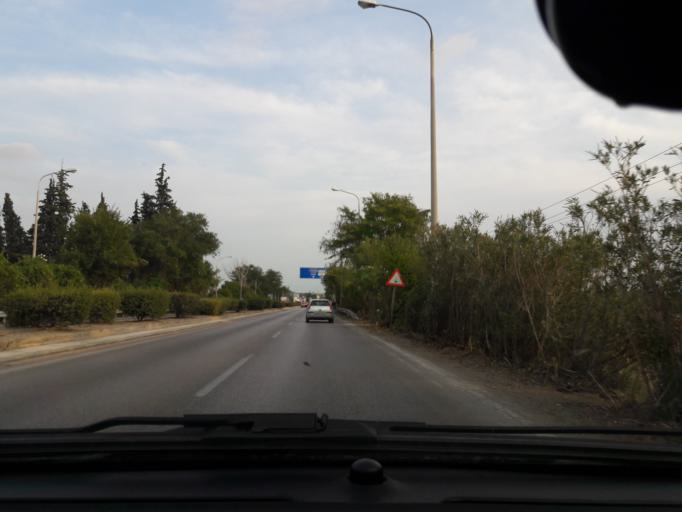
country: GR
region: Central Macedonia
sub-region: Nomos Thessalonikis
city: Thermi
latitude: 40.5354
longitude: 22.9926
